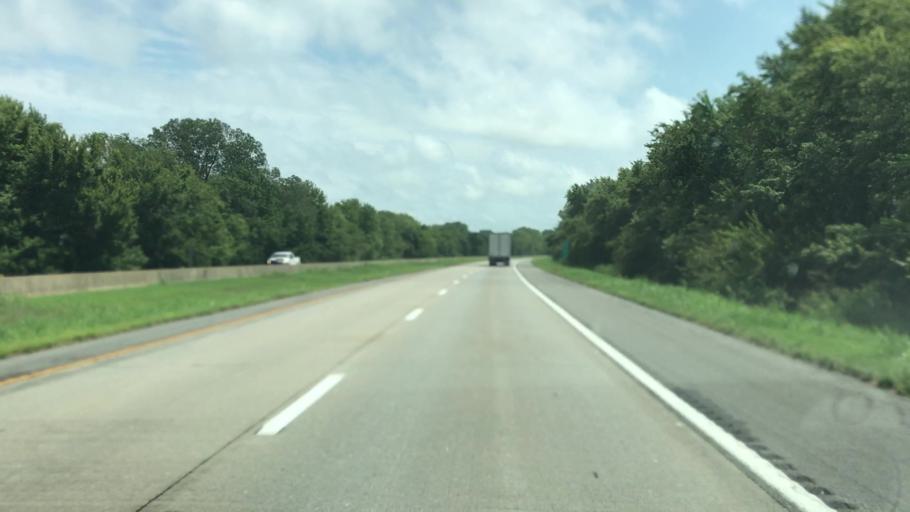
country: US
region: Missouri
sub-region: Pemiscot County
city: Caruthersville
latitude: 36.1322
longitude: -89.6249
